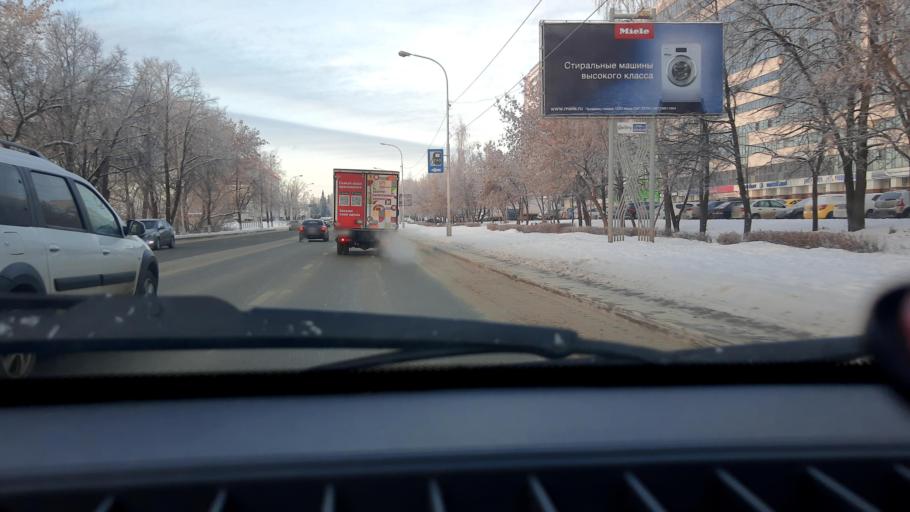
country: RU
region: Bashkortostan
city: Ufa
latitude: 54.8104
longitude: 56.0620
